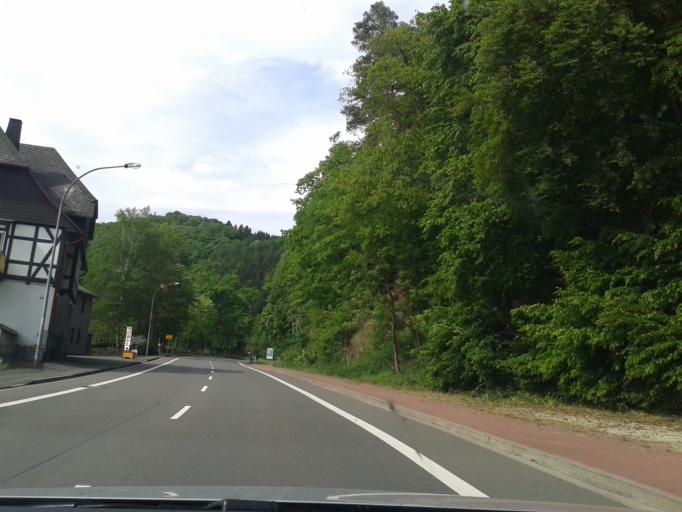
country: DE
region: Hesse
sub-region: Regierungsbezirk Kassel
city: Vohl
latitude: 51.1862
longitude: 8.8949
